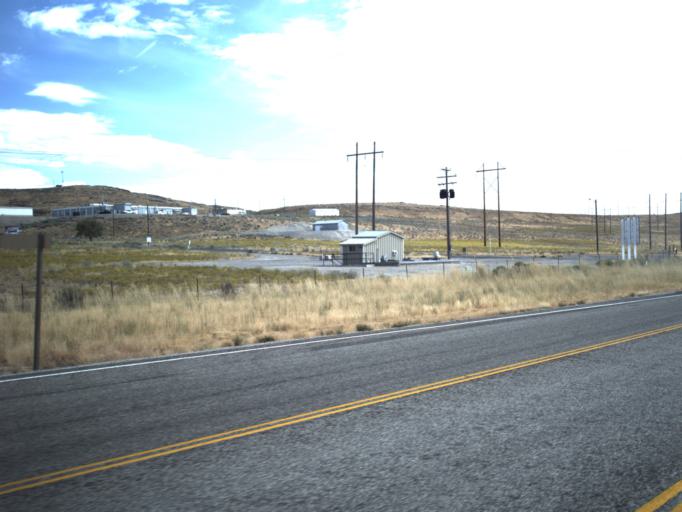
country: US
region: Utah
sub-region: Box Elder County
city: Tremonton
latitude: 41.6374
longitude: -112.4247
